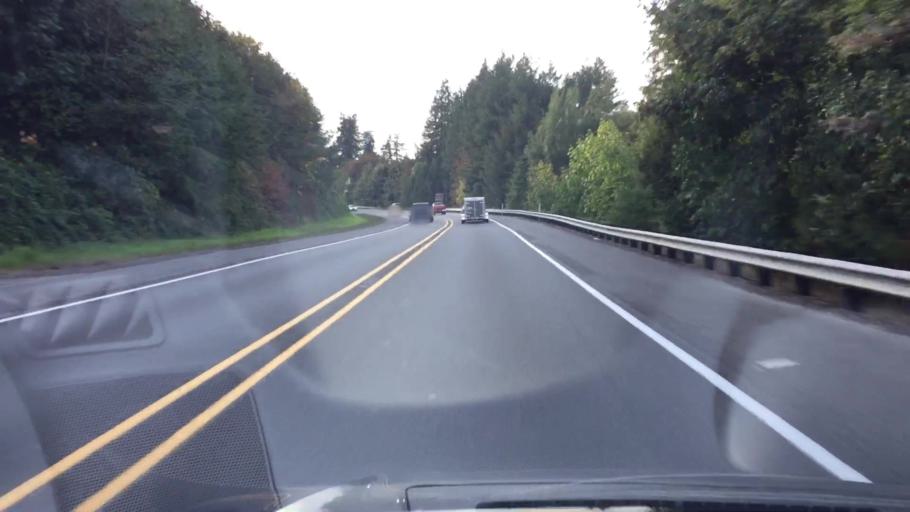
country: US
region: Washington
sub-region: Lewis County
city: Morton
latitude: 46.5344
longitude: -122.5397
